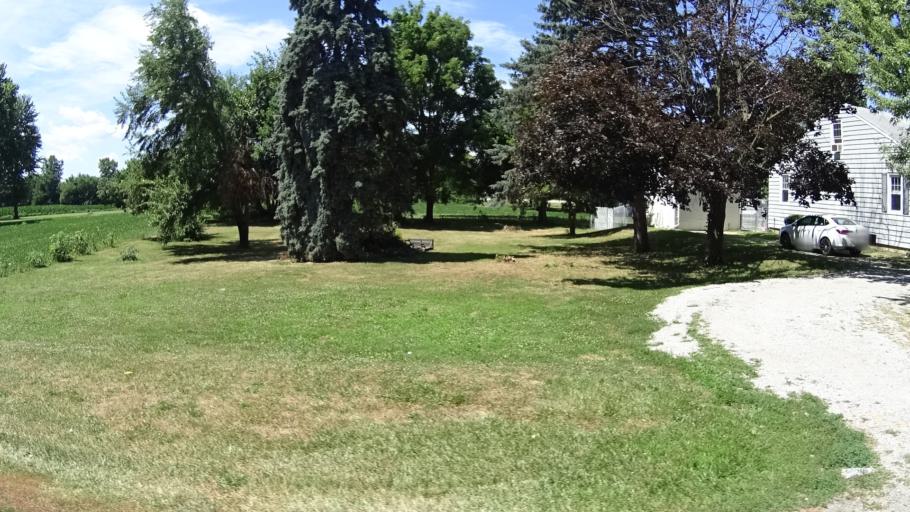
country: US
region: Ohio
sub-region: Erie County
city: Sandusky
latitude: 41.4068
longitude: -82.6818
